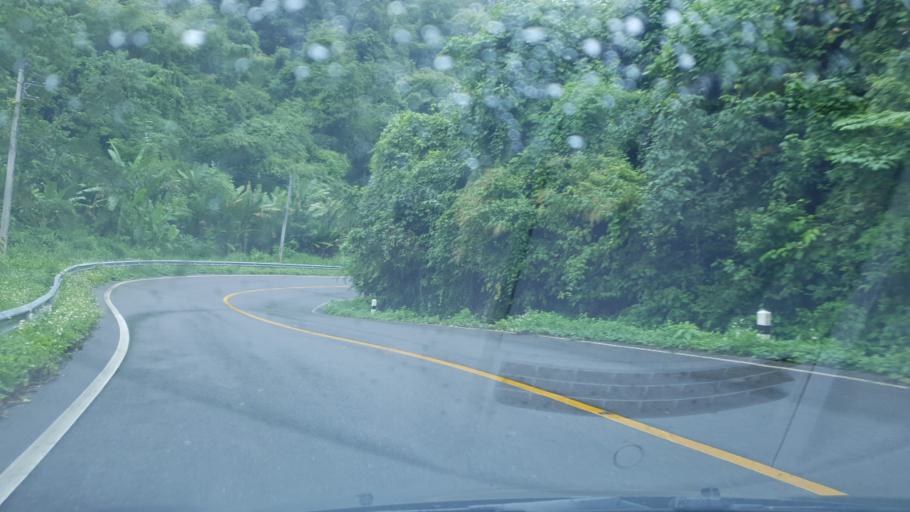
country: TH
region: Mae Hong Son
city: Mae La Noi
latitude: 18.5823
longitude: 97.9414
